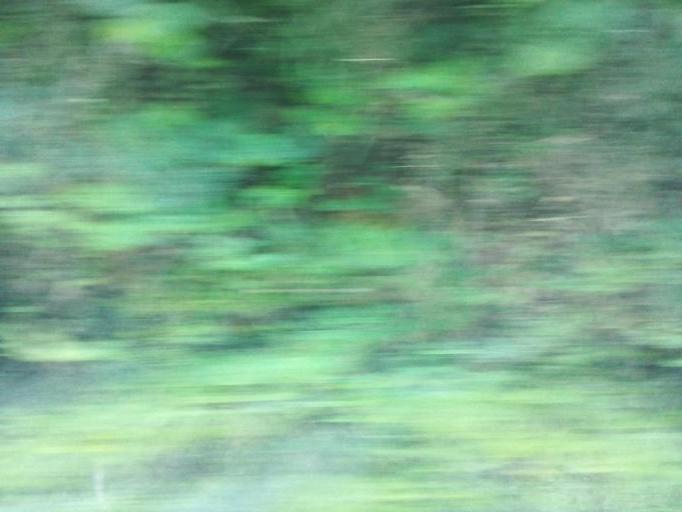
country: BR
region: Minas Gerais
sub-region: Joao Monlevade
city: Joao Monlevade
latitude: -19.8253
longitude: -43.1091
